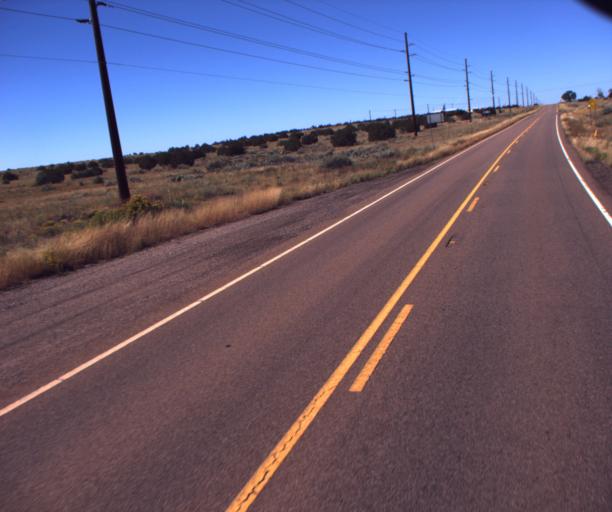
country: US
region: Arizona
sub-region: Navajo County
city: Taylor
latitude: 34.4853
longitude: -110.2458
